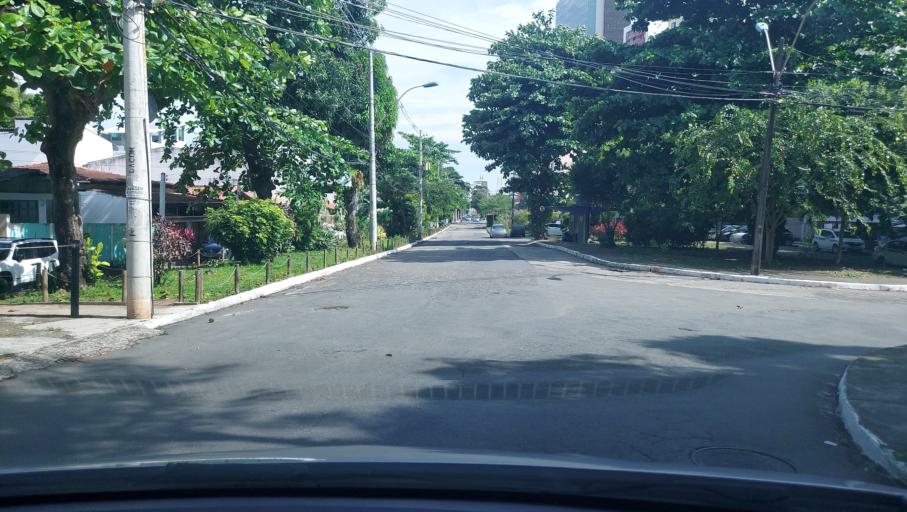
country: BR
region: Bahia
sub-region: Salvador
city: Salvador
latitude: -12.9846
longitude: -38.4487
